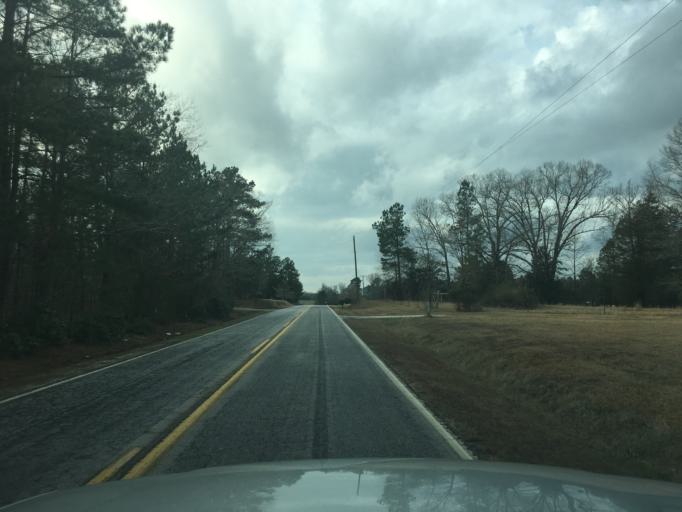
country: US
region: South Carolina
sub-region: Abbeville County
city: Abbeville
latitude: 34.2417
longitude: -82.4048
